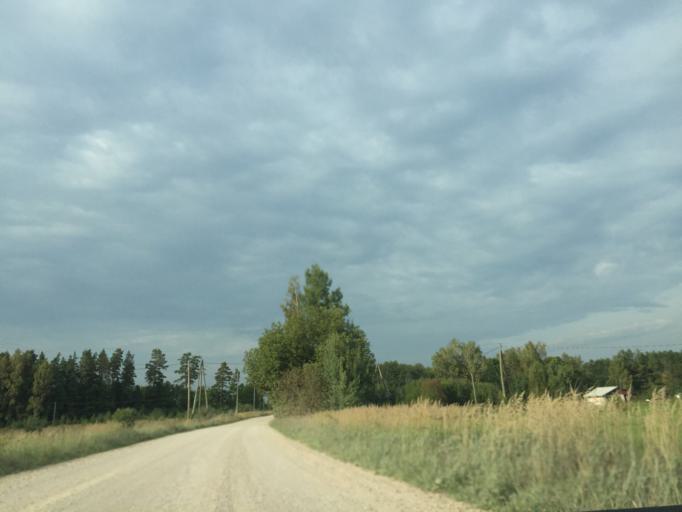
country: LV
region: Ikskile
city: Ikskile
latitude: 56.8118
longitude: 24.4475
